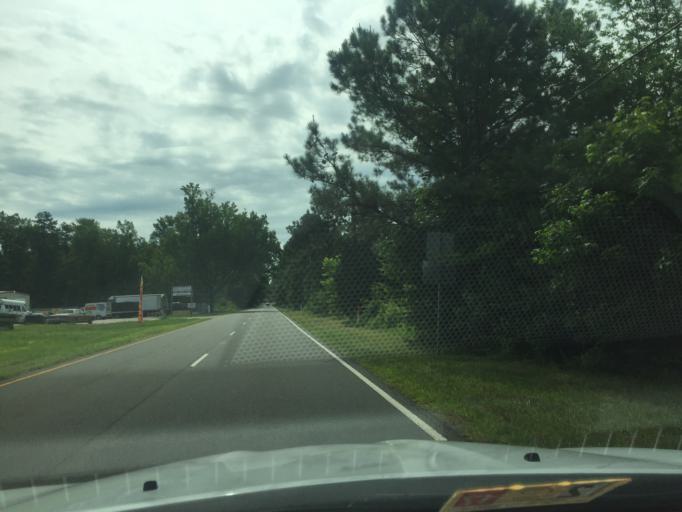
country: US
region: Virginia
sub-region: Charles City County
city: Charles City
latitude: 37.4484
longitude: -77.0695
